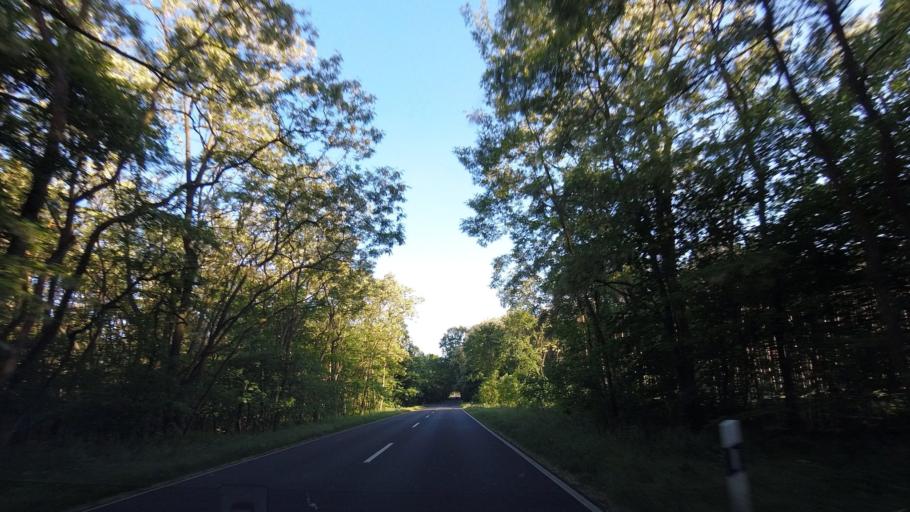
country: DE
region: Brandenburg
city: Golzow
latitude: 52.3201
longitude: 12.6074
